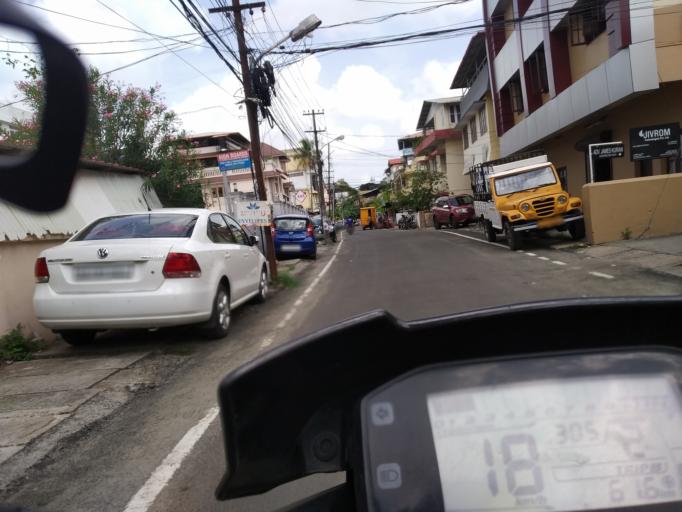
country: IN
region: Kerala
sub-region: Ernakulam
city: Cochin
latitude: 9.9901
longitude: 76.2842
